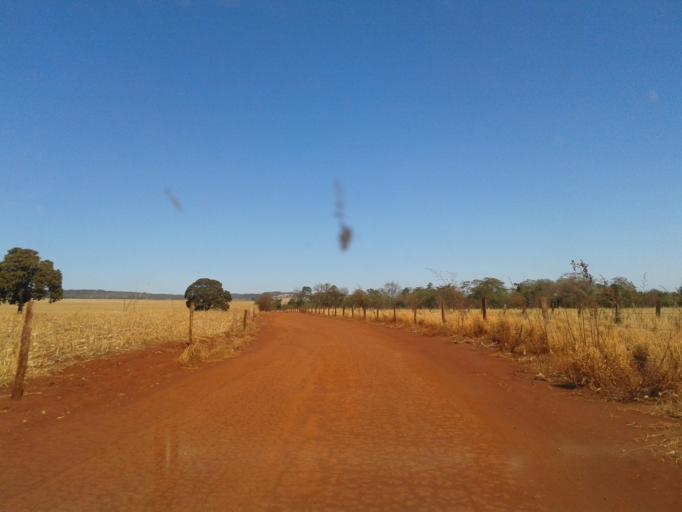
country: BR
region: Minas Gerais
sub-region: Centralina
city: Centralina
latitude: -18.5860
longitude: -49.1463
